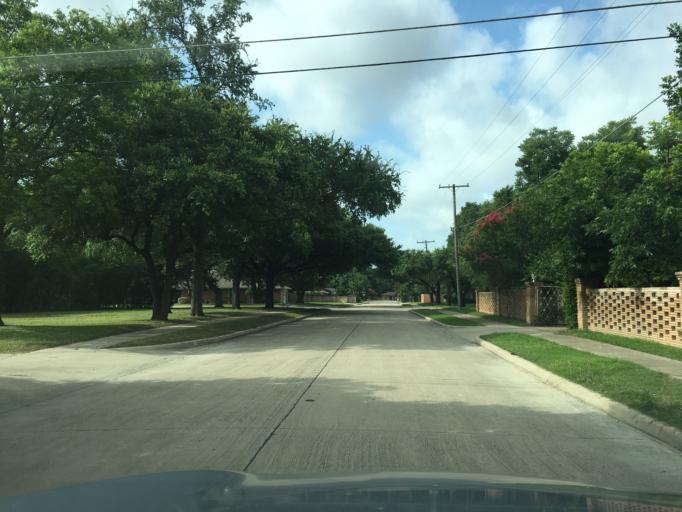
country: US
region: Texas
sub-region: Dallas County
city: Richardson
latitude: 32.9500
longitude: -96.7260
